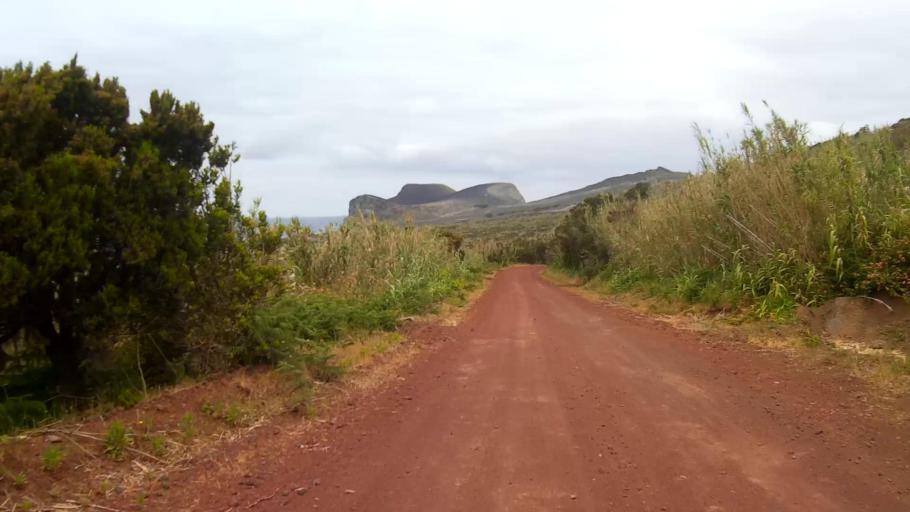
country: PT
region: Azores
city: Ribeira Grande
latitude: 38.5854
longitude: -28.8177
